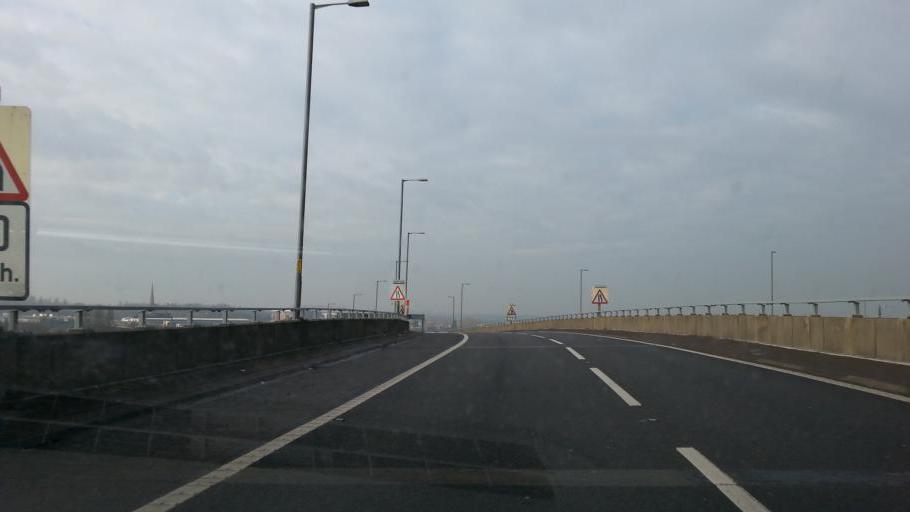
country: GB
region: England
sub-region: City and Borough of Birmingham
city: Birmingham
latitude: 52.5099
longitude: -1.8646
